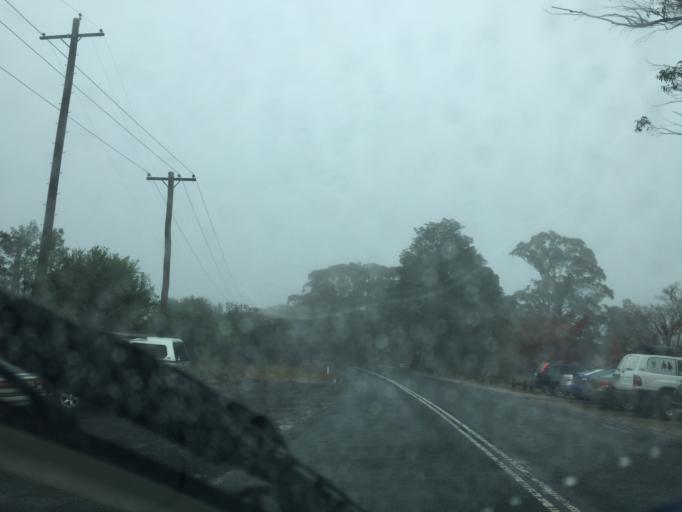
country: AU
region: New South Wales
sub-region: Blue Mountains Municipality
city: Leura
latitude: -33.7054
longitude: 150.3695
